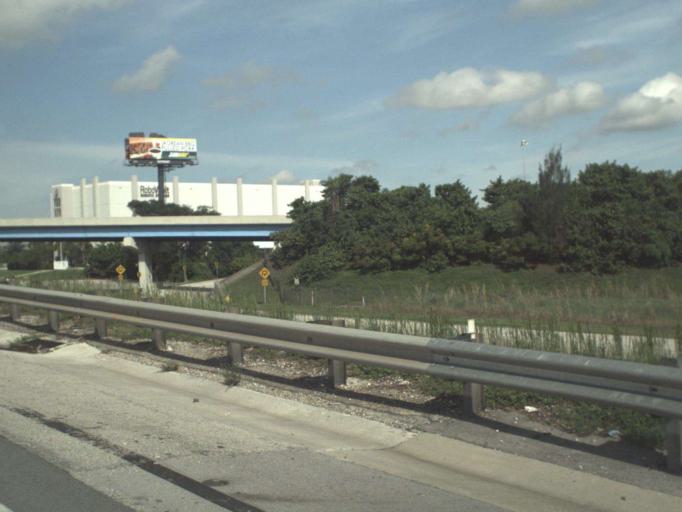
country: US
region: Florida
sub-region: Broward County
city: Dania Beach
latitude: 26.0810
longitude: -80.1355
